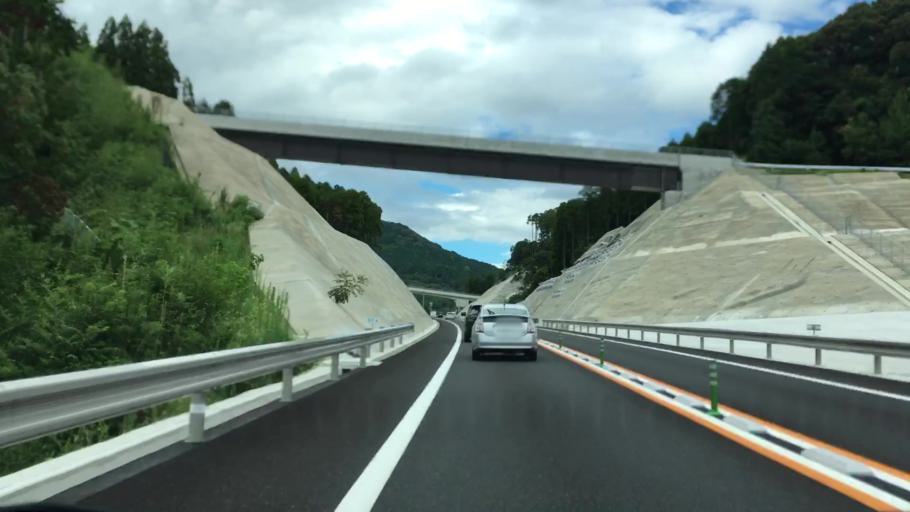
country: JP
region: Saga Prefecture
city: Imaricho-ko
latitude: 33.3033
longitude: 129.9158
